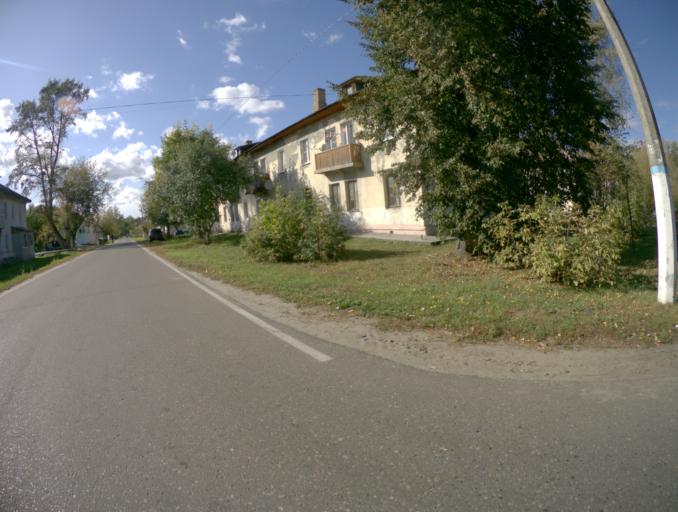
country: RU
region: Moskovskaya
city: Kerva
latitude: 55.6101
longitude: 39.5781
